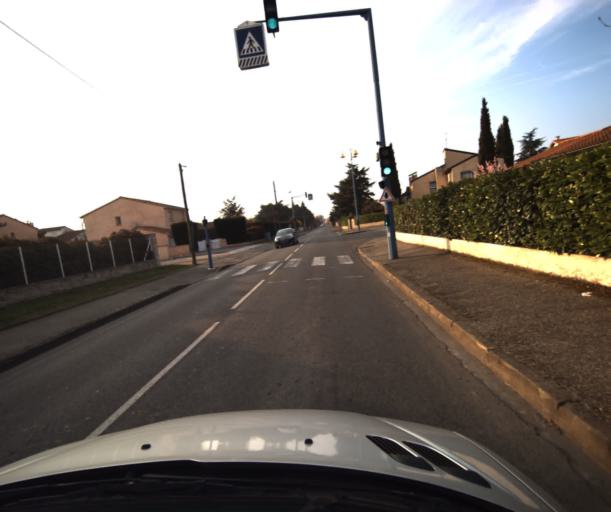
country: FR
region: Midi-Pyrenees
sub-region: Departement de la Haute-Garonne
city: Castelginest
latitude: 43.6882
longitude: 1.4362
